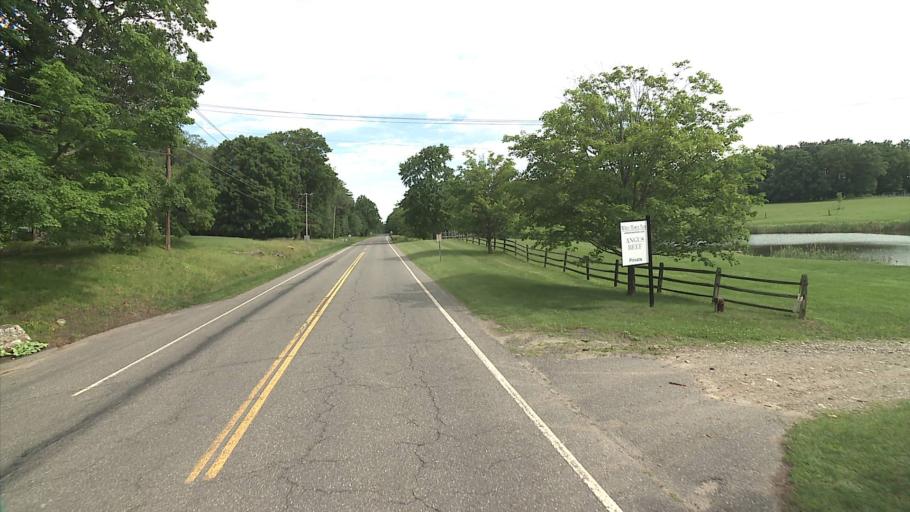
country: US
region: Connecticut
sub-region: Litchfield County
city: Litchfield
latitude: 41.6998
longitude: -73.1839
